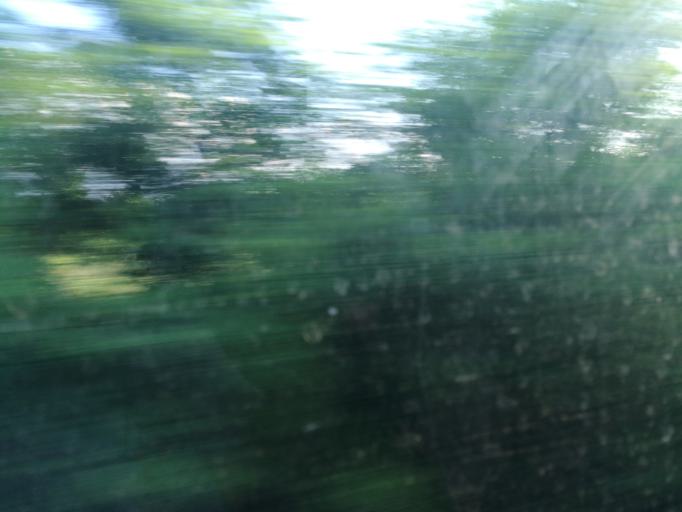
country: RO
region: Arges
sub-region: Comuna Calinesti
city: Calinesti
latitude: 44.8195
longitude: 25.0345
